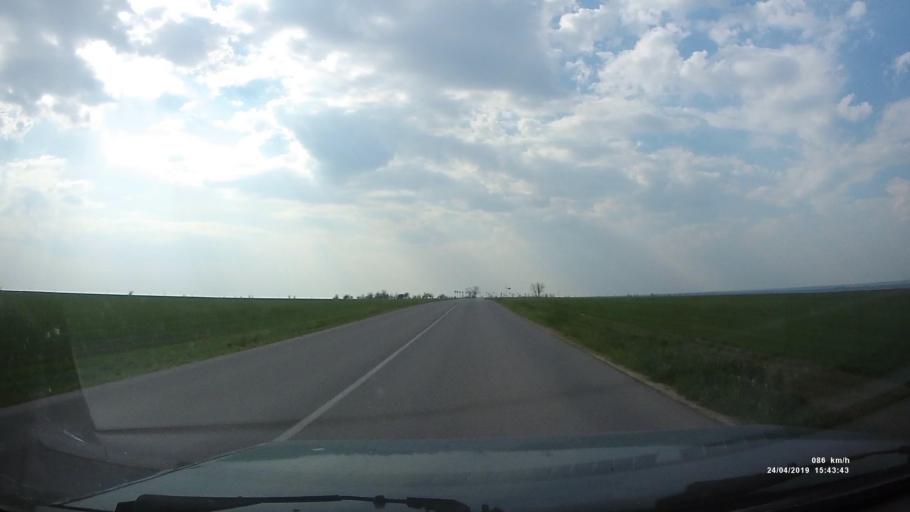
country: RU
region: Kalmykiya
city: Yashalta
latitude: 46.5843
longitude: 42.7675
